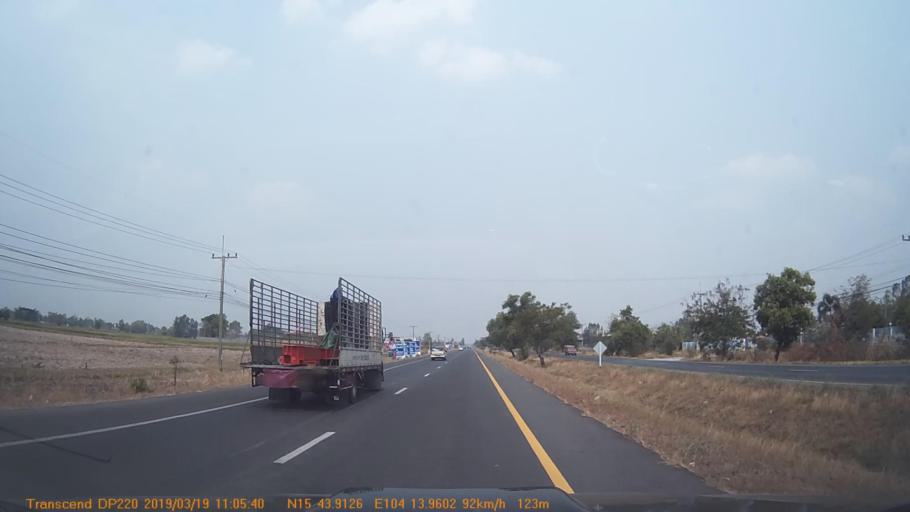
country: TH
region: Yasothon
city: Yasothon
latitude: 15.7320
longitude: 104.2326
